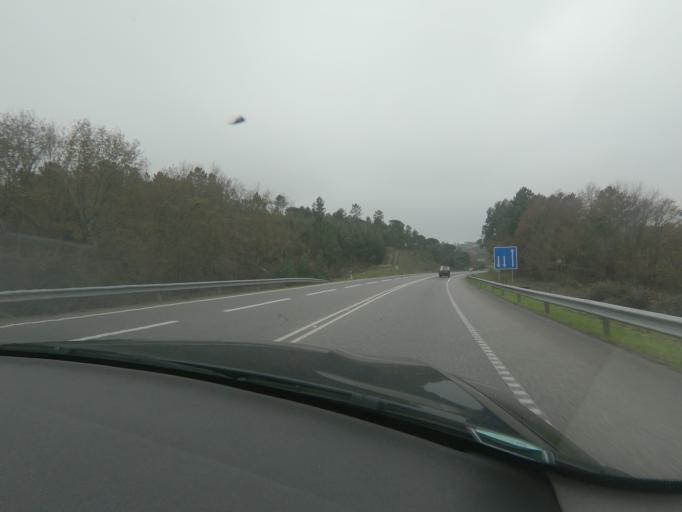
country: PT
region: Viseu
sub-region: Concelho de Tondela
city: Tondela
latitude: 40.5805
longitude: -8.0207
